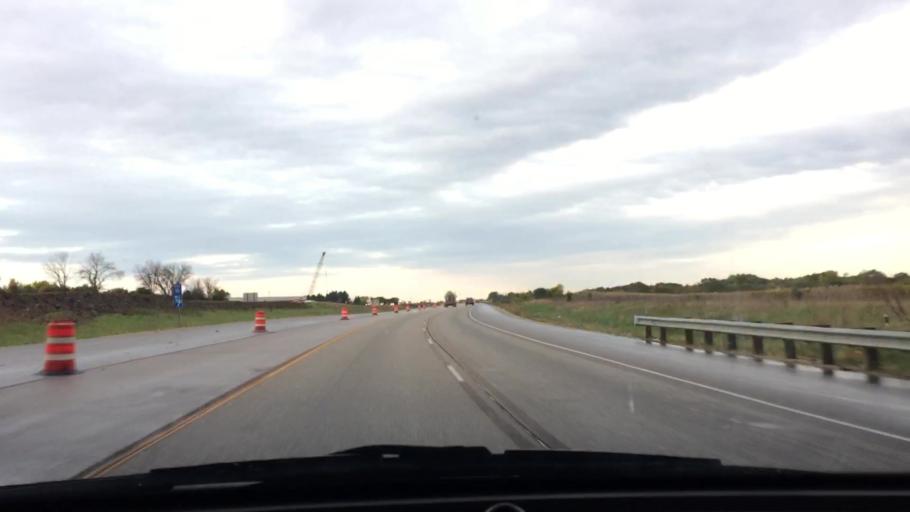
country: US
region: Wisconsin
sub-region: Rock County
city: Beloit
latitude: 42.5141
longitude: -88.9785
